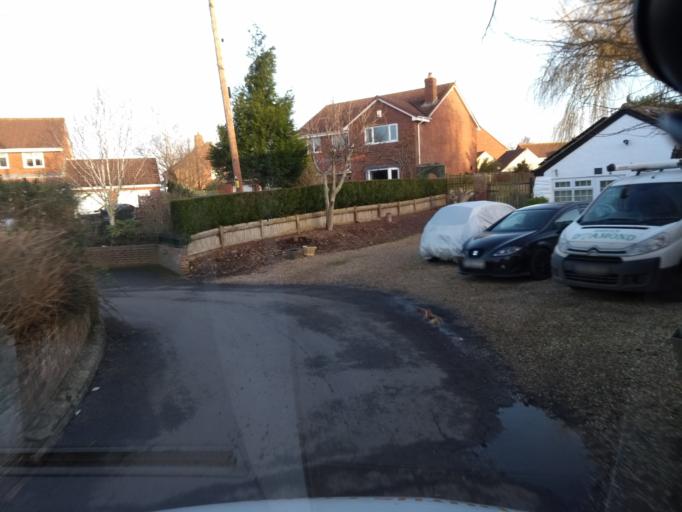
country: GB
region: England
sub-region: Somerset
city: Bridgwater
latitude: 51.1477
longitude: -3.0068
